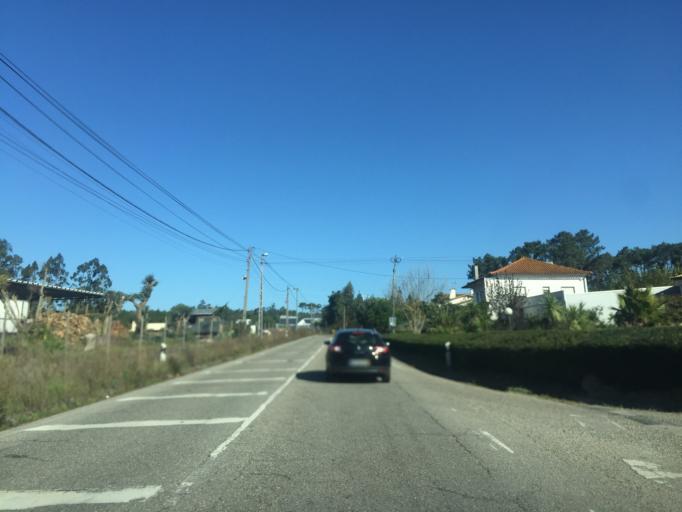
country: PT
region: Leiria
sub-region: Leiria
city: Amor
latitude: 39.8151
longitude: -8.8429
